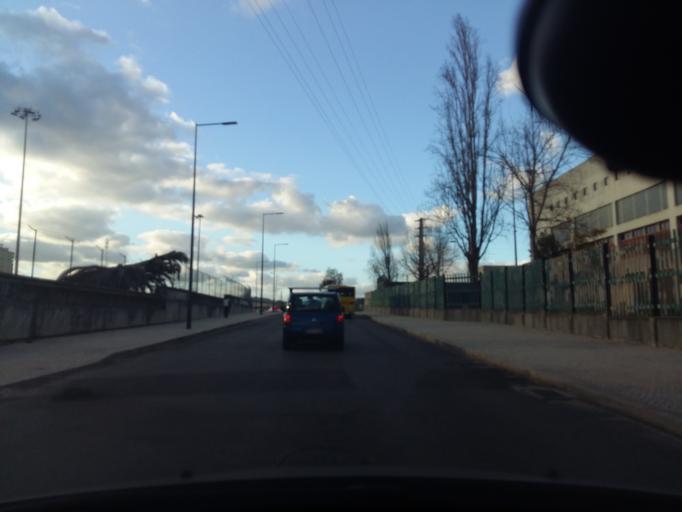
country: PT
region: Lisbon
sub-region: Odivelas
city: Pontinha
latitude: 38.7620
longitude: -9.1936
